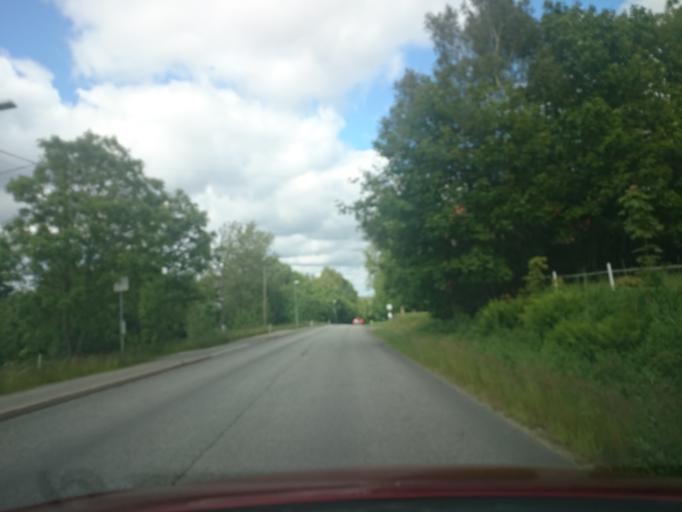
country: SE
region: Vaestra Goetaland
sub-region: Harryda Kommun
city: Landvetter
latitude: 57.7010
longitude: 12.1875
